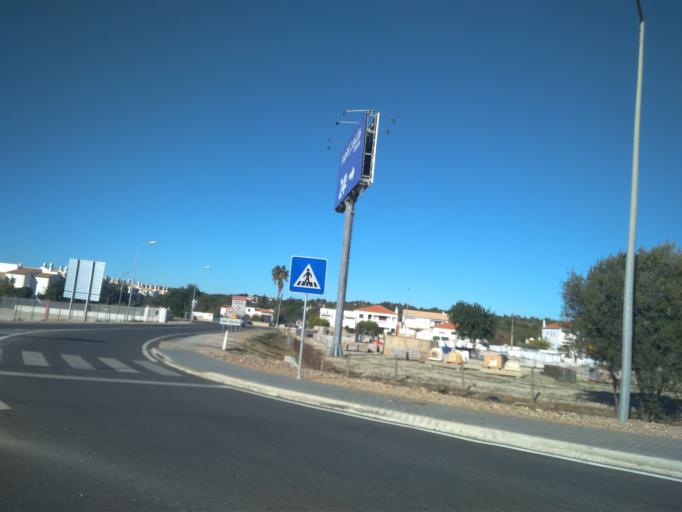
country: PT
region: Faro
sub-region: Albufeira
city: Ferreiras
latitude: 37.1233
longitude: -8.2238
